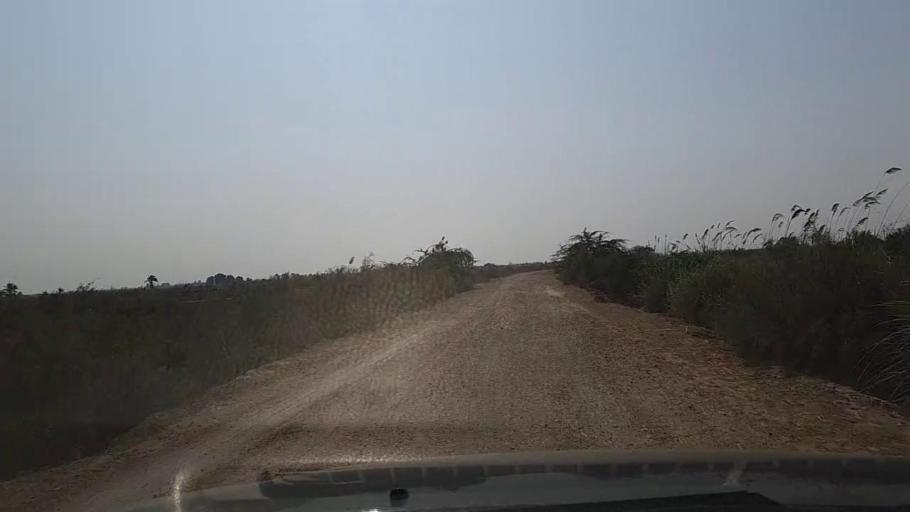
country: PK
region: Sindh
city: Mirpur Sakro
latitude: 24.3820
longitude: 67.6614
